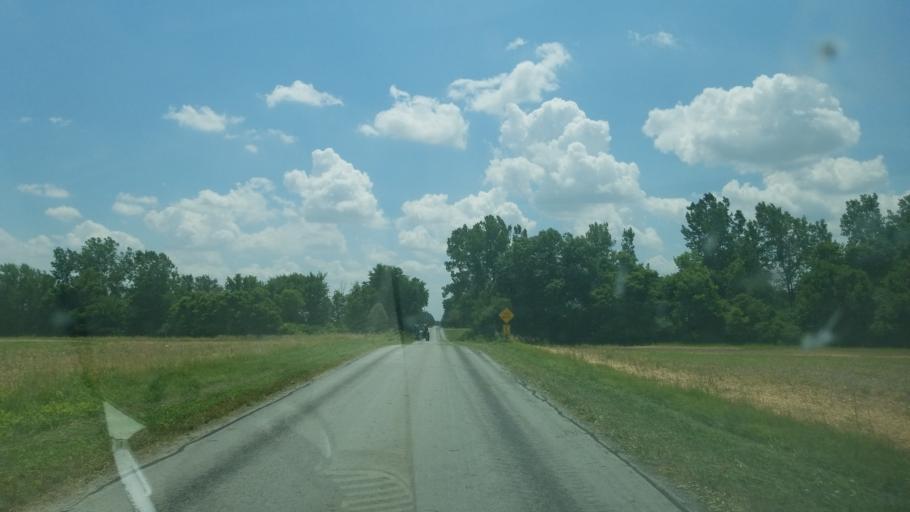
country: US
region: Ohio
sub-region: Hardin County
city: Kenton
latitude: 40.6271
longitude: -83.5608
